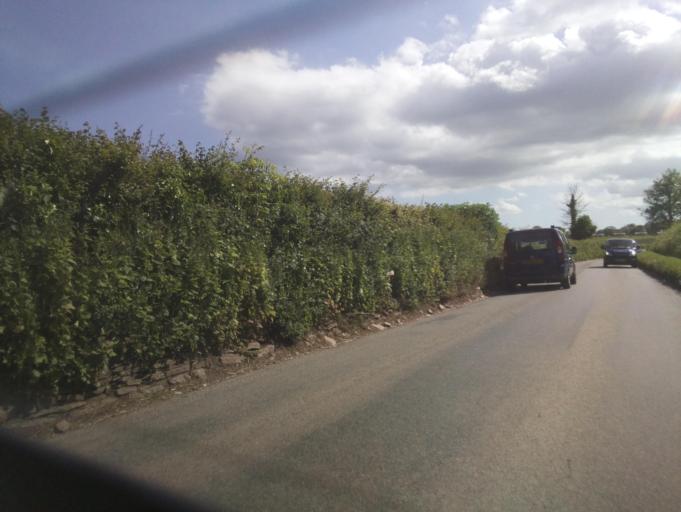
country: GB
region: England
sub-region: Devon
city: Totnes
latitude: 50.4361
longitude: -3.6538
